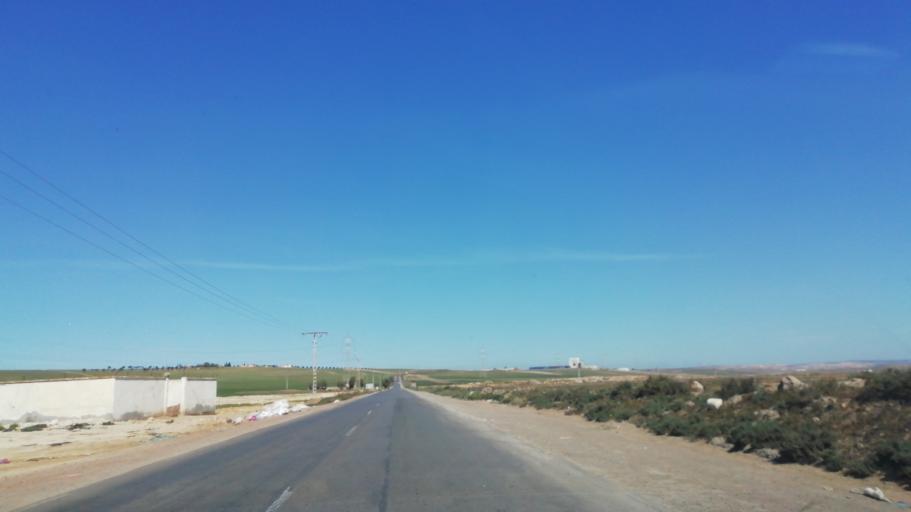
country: DZ
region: Oran
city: Es Senia
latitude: 35.5294
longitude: -0.5863
